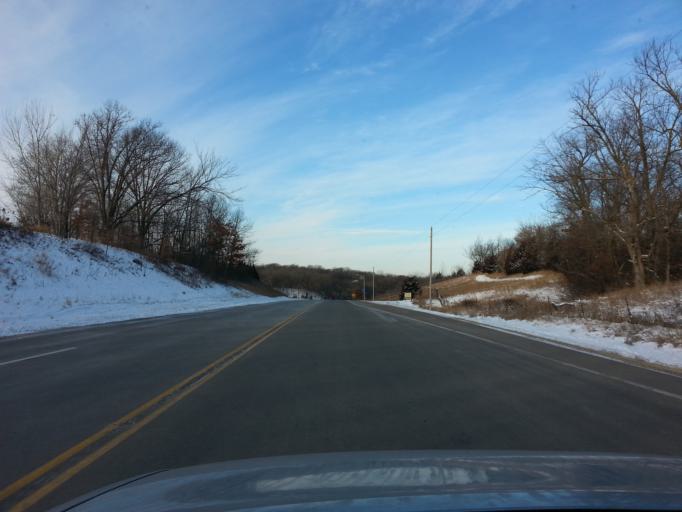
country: US
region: Minnesota
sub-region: Scott County
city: Prior Lake
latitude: 44.7610
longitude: -93.3968
